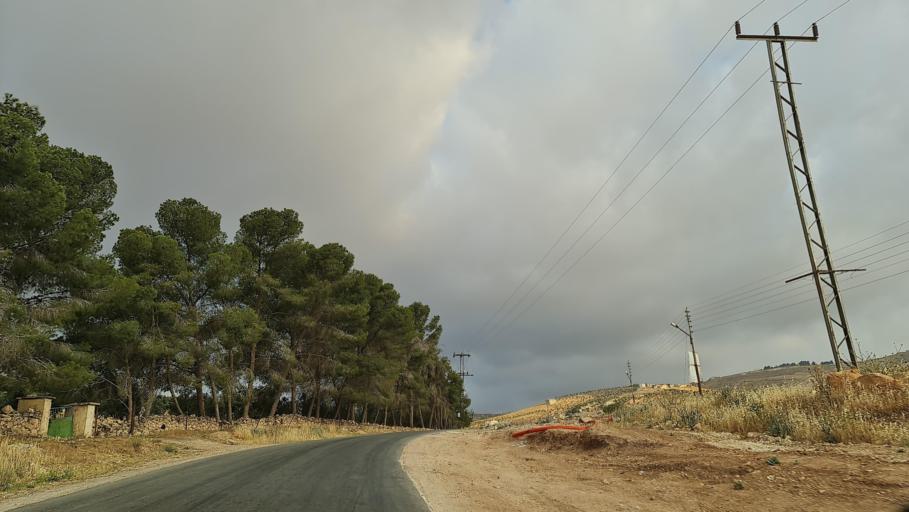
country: JO
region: Amman
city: Al Jubayhah
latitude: 32.0913
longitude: 35.9321
